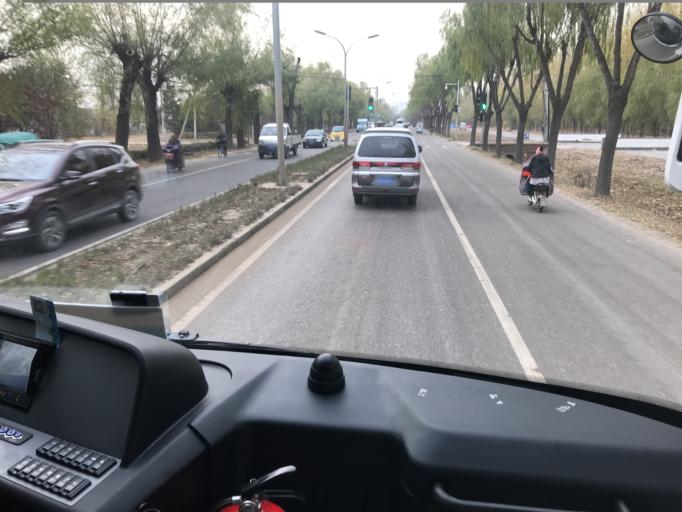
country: CN
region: Beijing
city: Wenquan
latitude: 40.0868
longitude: 116.2101
